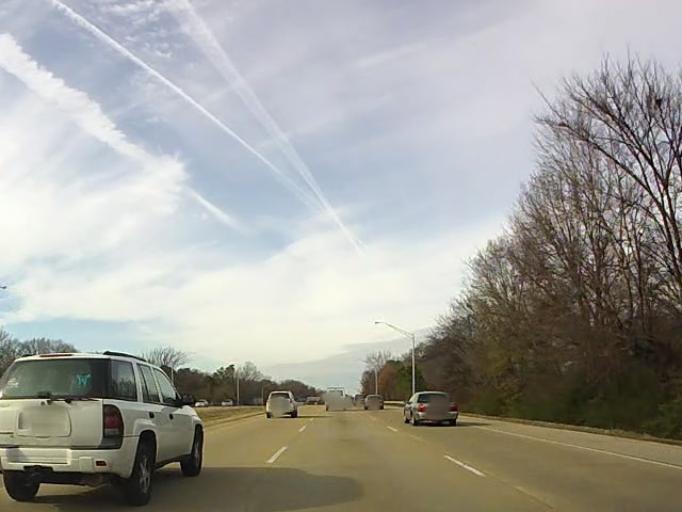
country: US
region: Tennessee
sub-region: Shelby County
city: Bartlett
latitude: 35.1458
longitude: -89.9158
